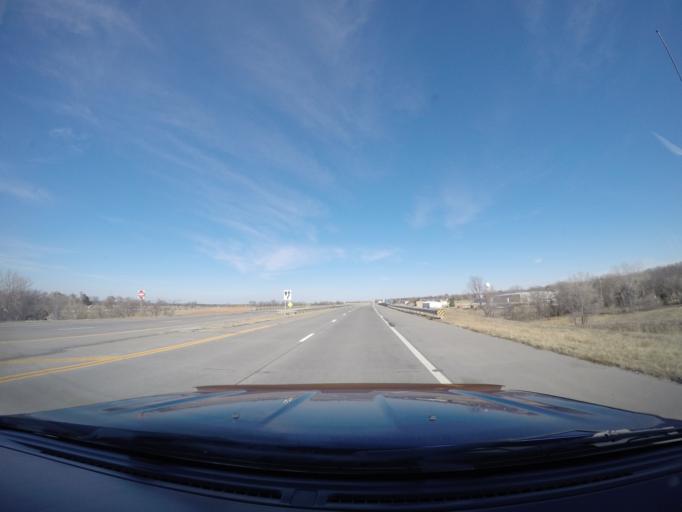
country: US
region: Kansas
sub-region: Republic County
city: Belleville
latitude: 39.8256
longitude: -97.6385
